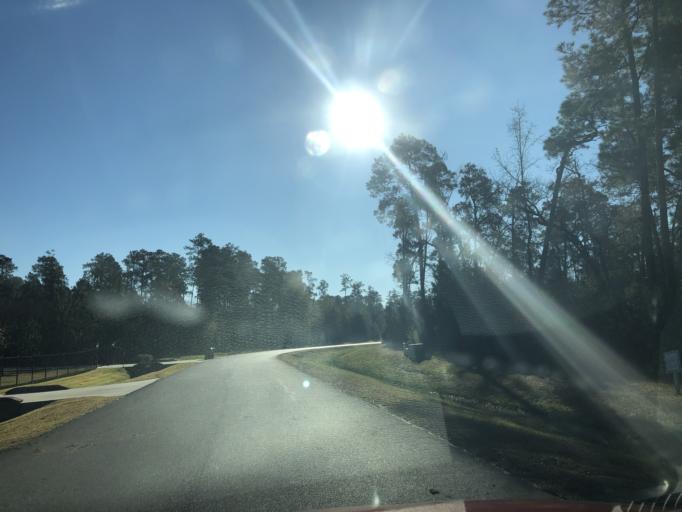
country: US
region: Texas
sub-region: Montgomery County
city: Porter Heights
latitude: 30.0802
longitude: -95.3219
